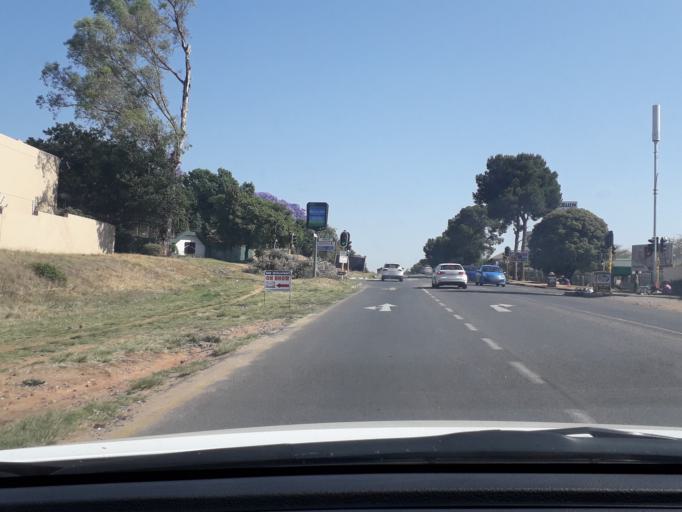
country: ZA
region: Gauteng
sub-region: City of Johannesburg Metropolitan Municipality
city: Roodepoort
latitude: -26.0884
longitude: 27.9583
